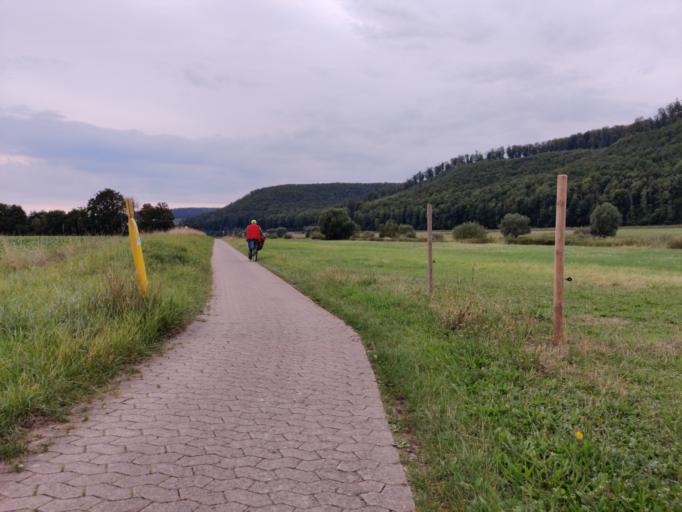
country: DE
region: Lower Saxony
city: Hehlen
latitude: 51.9938
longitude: 9.4367
